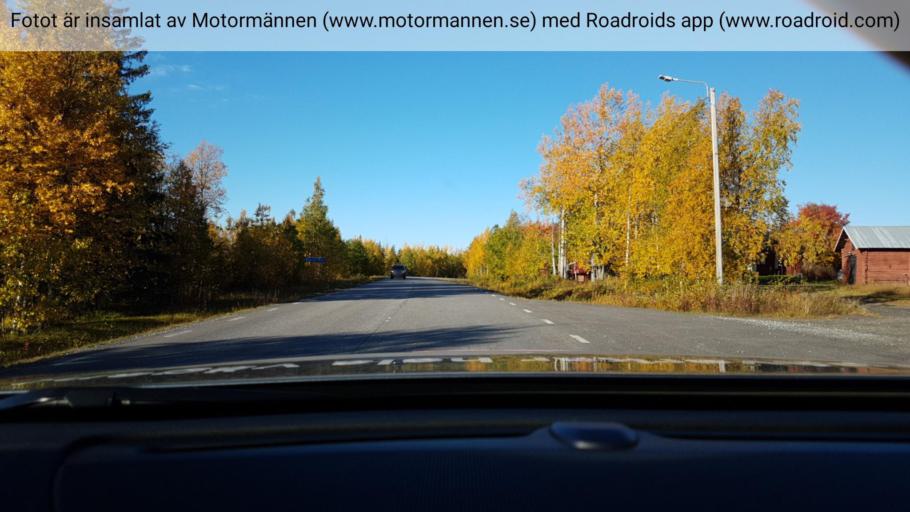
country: SE
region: Vaesterbotten
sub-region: Skelleftea Kommun
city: Storvik
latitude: 65.3612
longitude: 20.4376
